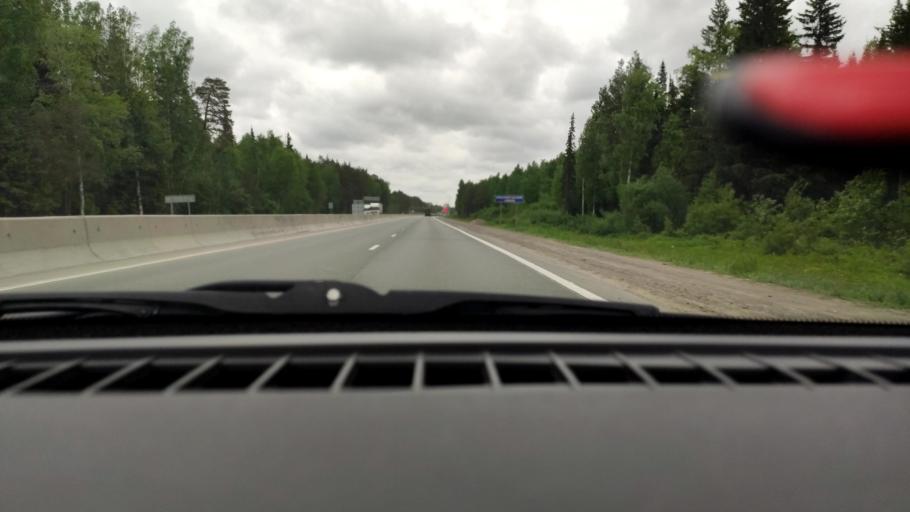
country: RU
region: Perm
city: Overyata
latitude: 58.0419
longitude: 55.8864
